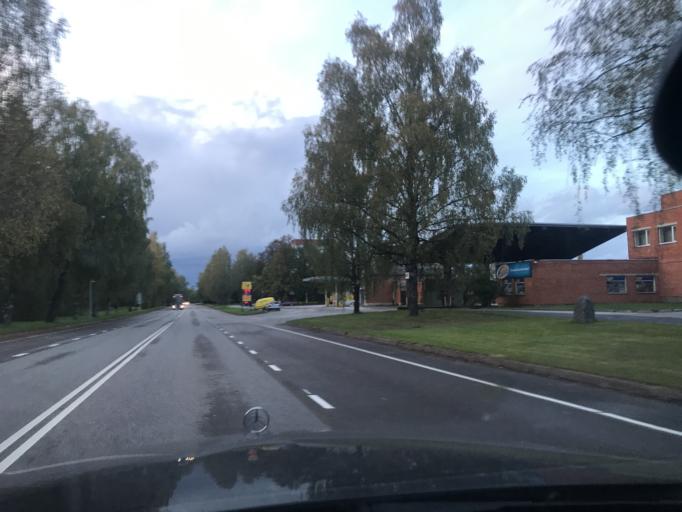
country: EE
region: Valgamaa
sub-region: Torva linn
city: Torva
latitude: 57.9897
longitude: 25.9401
